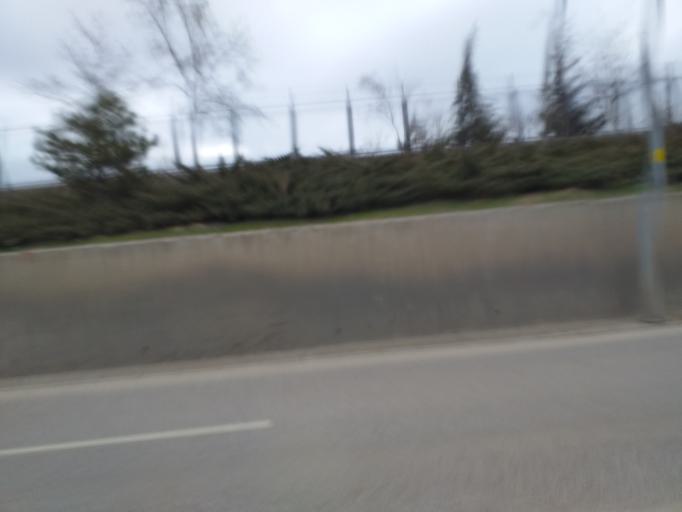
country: TR
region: Ankara
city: Ankara
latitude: 39.9628
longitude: 32.8215
